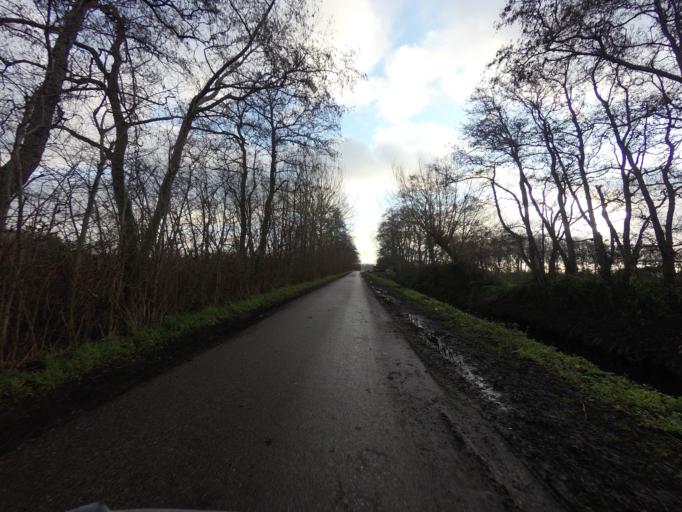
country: NL
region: North Holland
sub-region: Gemeente Texel
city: Den Burg
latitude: 53.0937
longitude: 4.7738
